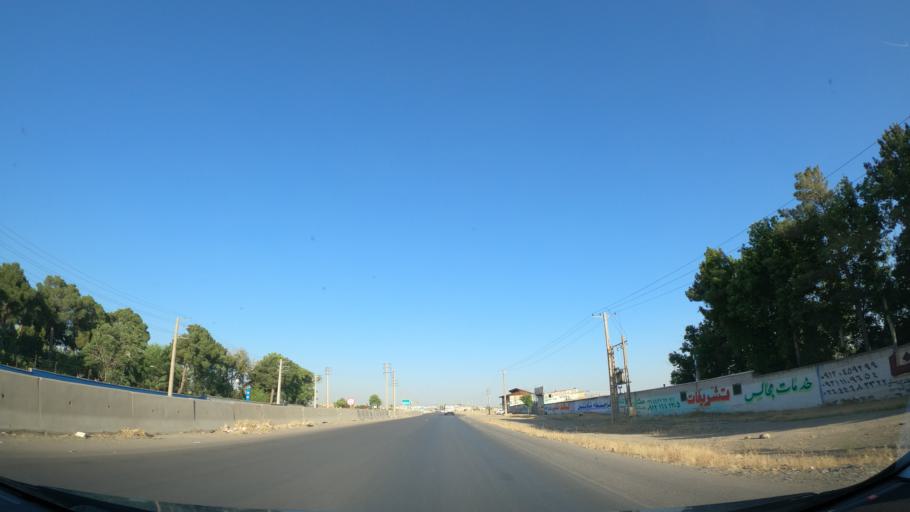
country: IR
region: Alborz
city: Hashtgerd
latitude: 35.9212
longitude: 50.7463
